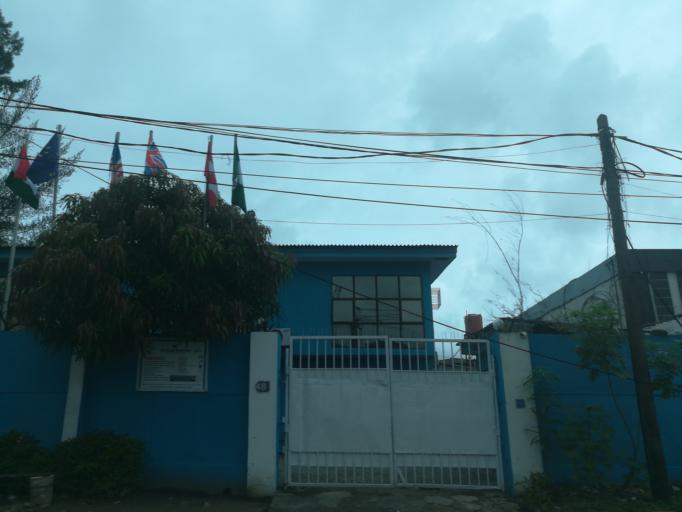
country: NG
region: Lagos
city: Ikoyi
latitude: 6.4270
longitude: 3.4218
